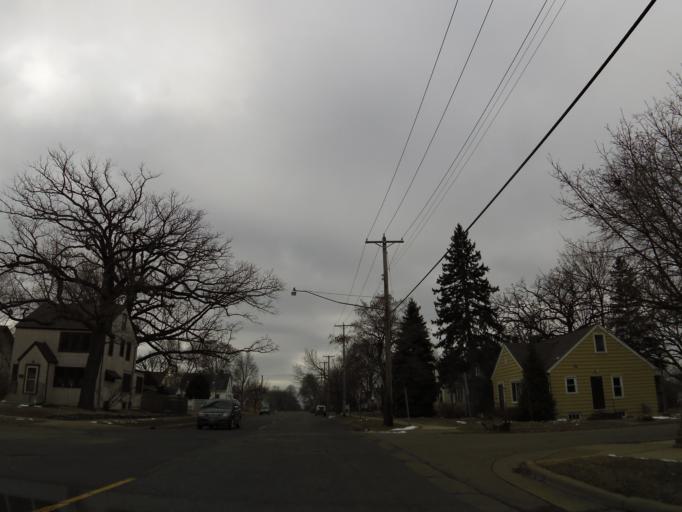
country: US
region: Minnesota
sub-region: Dakota County
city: Mendota Heights
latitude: 44.9218
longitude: -93.1569
